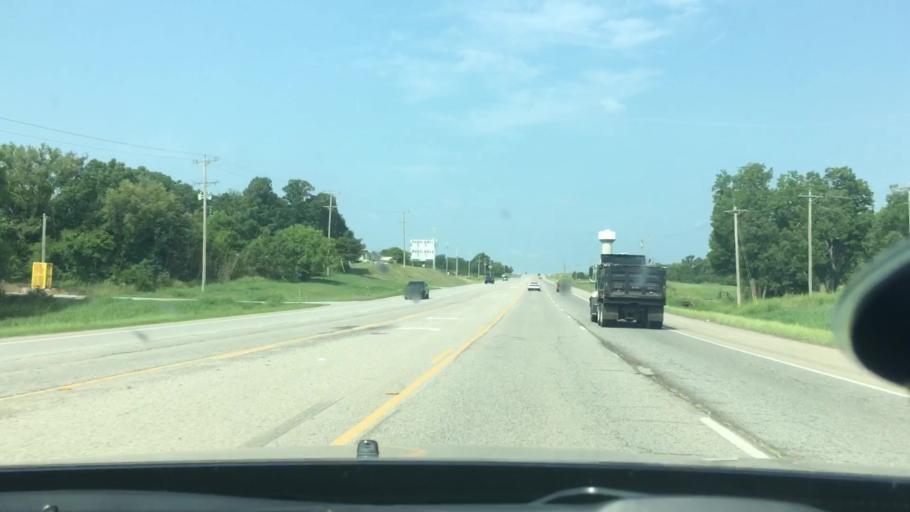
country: US
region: Oklahoma
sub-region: Bryan County
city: Calera
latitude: 33.9978
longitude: -96.4434
